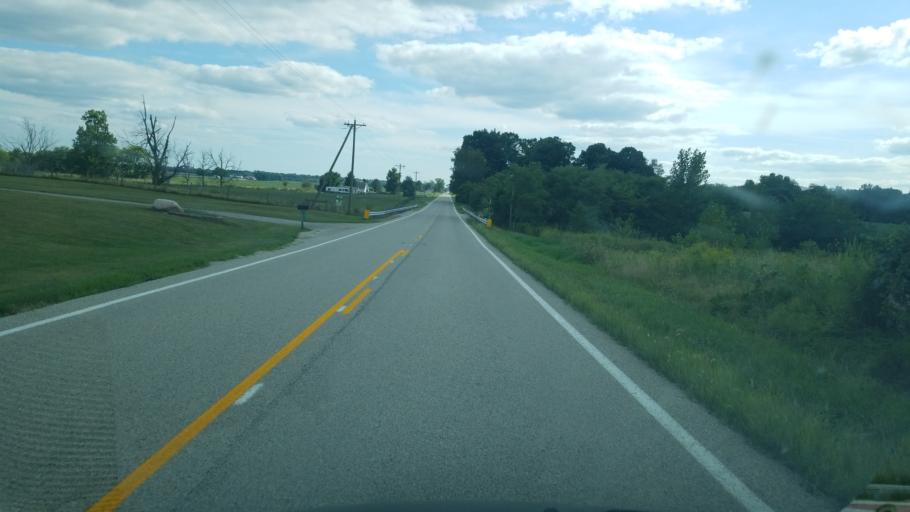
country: US
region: Ohio
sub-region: Logan County
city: De Graff
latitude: 40.2387
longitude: -83.9390
